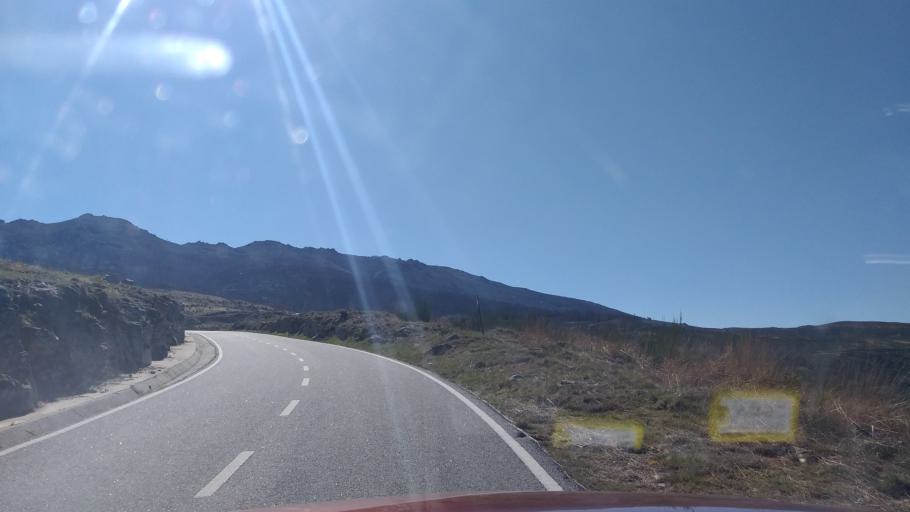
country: PT
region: Guarda
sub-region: Manteigas
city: Manteigas
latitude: 40.5002
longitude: -7.5207
